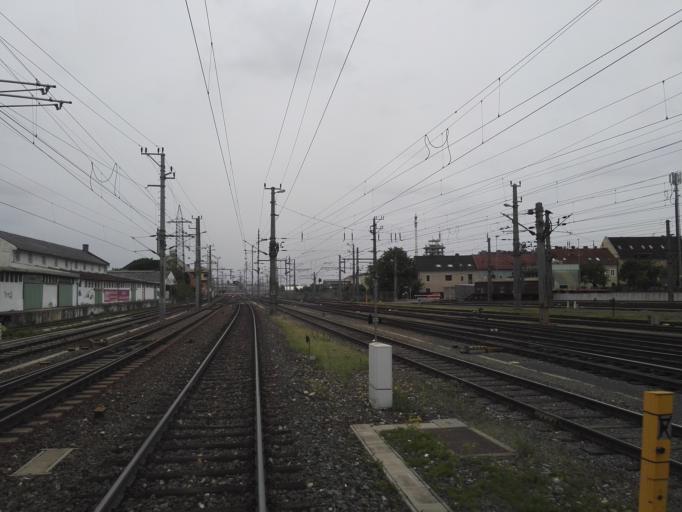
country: AT
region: Styria
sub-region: Graz Stadt
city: Goesting
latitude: 47.0847
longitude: 15.4103
